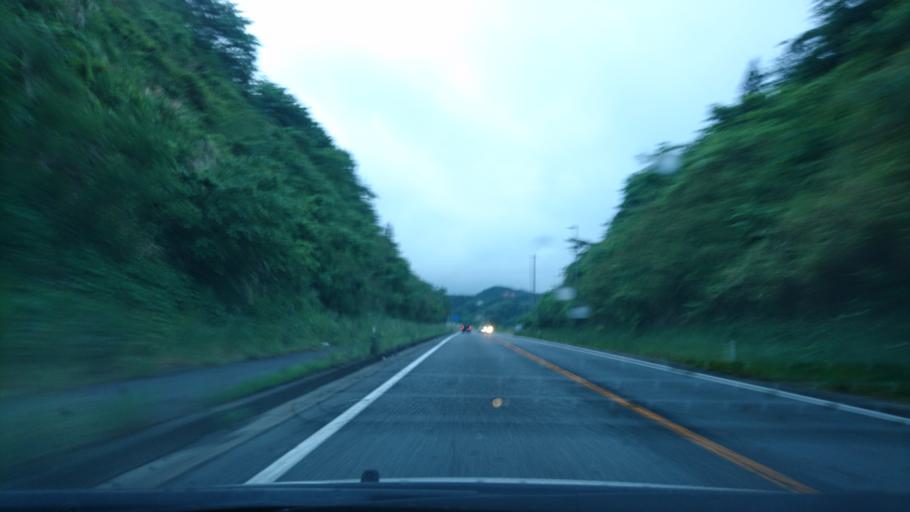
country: JP
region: Iwate
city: Ichinoseki
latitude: 38.8946
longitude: 141.1155
